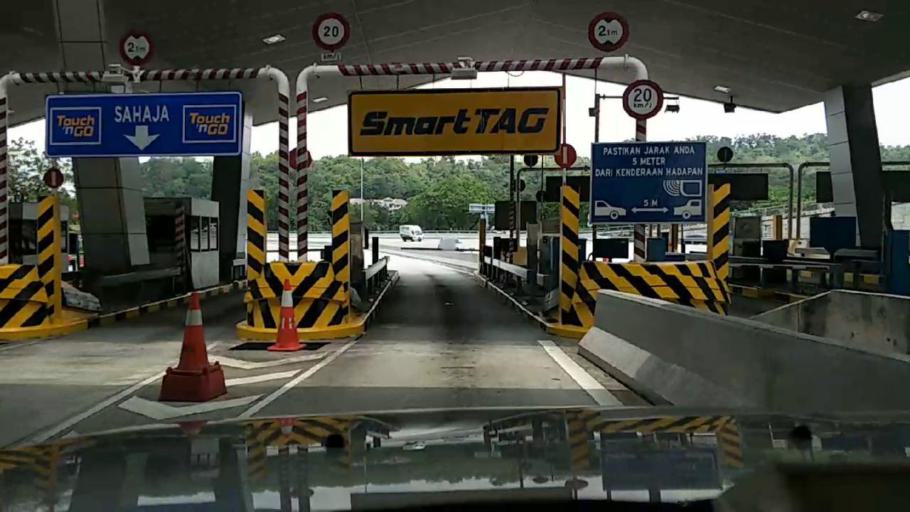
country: MY
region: Kuala Lumpur
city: Kuala Lumpur
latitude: 3.0933
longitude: 101.6707
